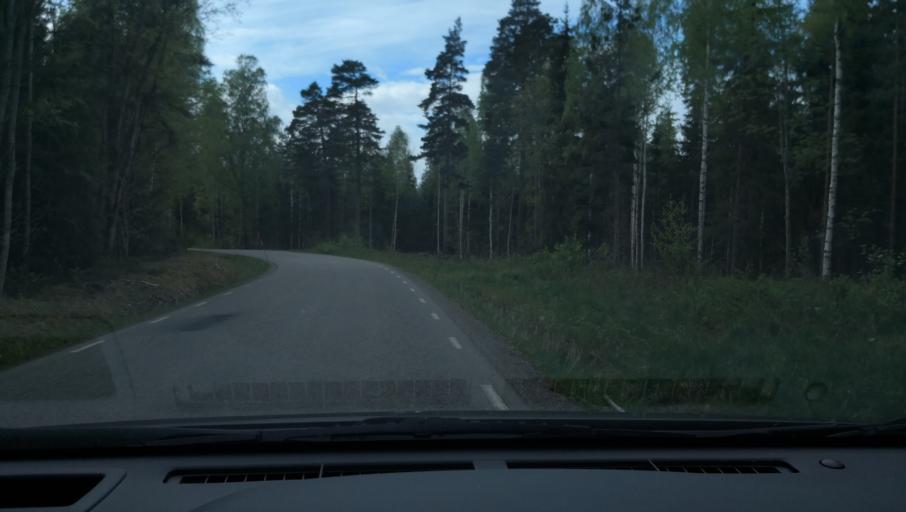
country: SE
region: OErebro
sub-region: Kumla Kommun
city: Hallabrottet
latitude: 59.1564
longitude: 15.1984
